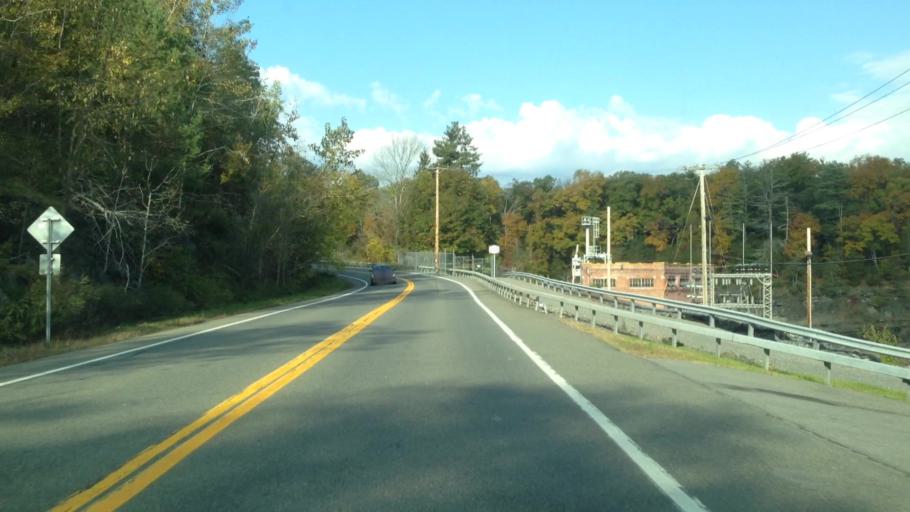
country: US
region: New York
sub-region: Ulster County
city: Tillson
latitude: 41.8211
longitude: -74.0482
